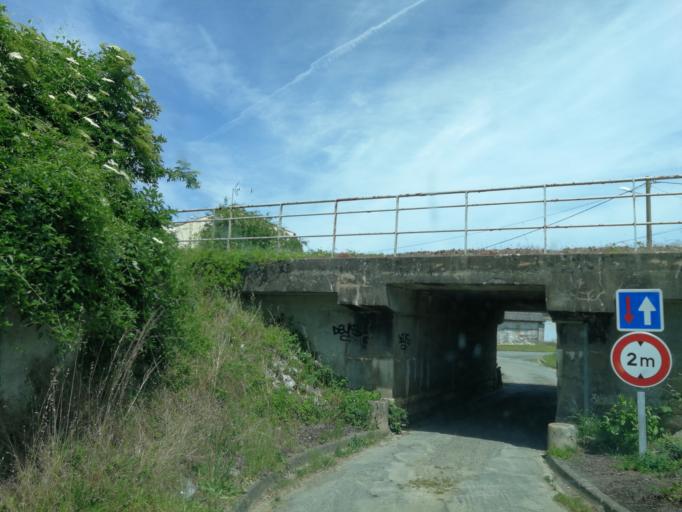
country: FR
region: Pays de la Loire
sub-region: Departement de la Vendee
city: Le Langon
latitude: 46.4185
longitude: -0.9067
